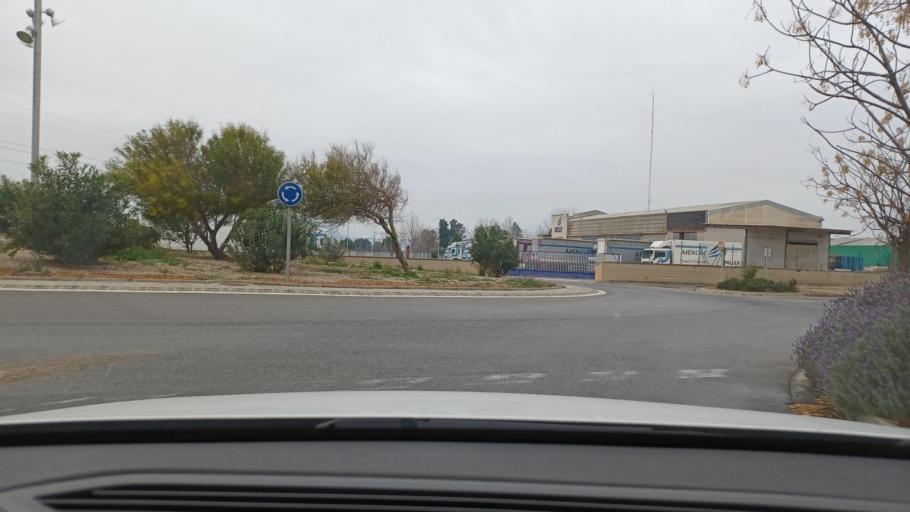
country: ES
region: Catalonia
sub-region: Provincia de Tarragona
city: Amposta
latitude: 40.7557
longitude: 0.6001
